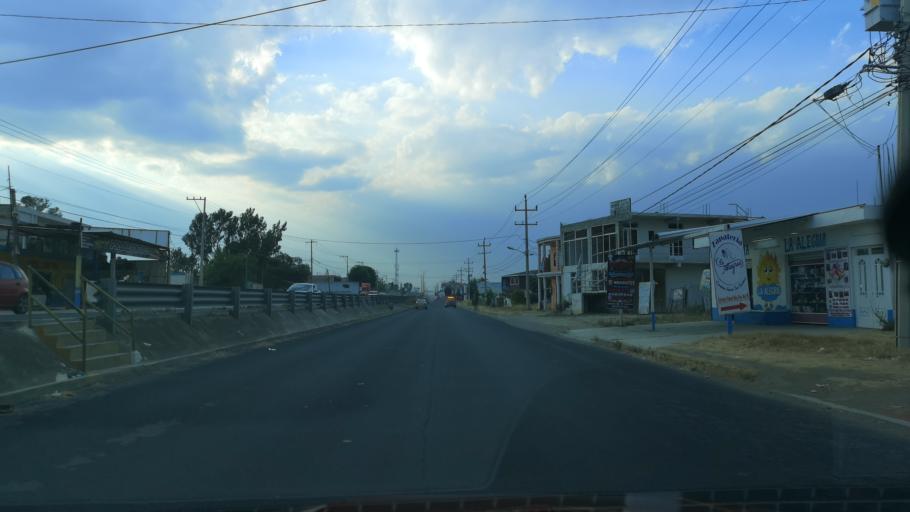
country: MX
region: Puebla
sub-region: Juan C. Bonilla
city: Santa Maria Zacatepec
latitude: 19.1159
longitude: -98.3589
